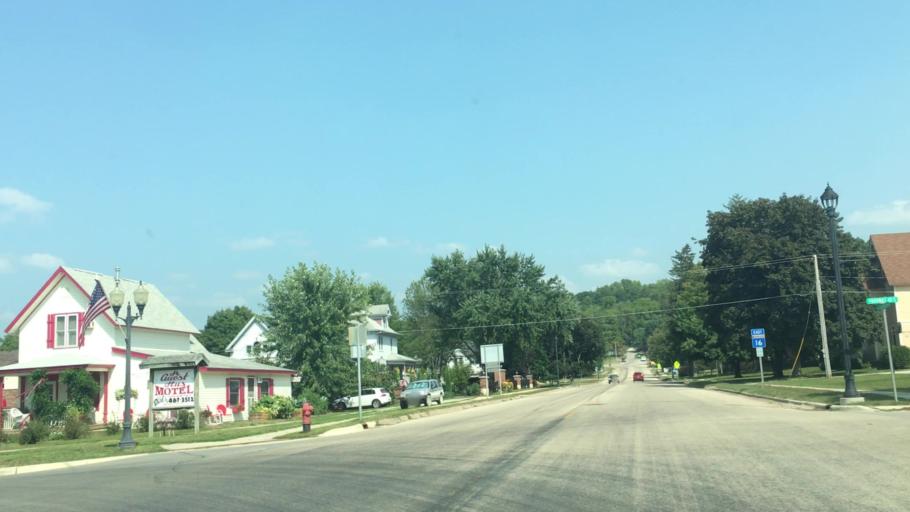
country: US
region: Minnesota
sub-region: Fillmore County
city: Preston
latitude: 43.7140
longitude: -91.9771
